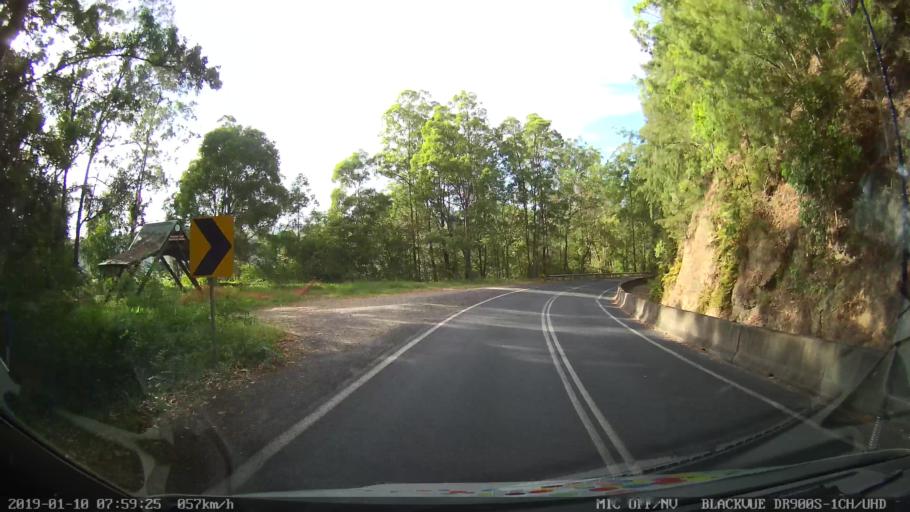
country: AU
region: New South Wales
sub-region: Bellingen
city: Dorrigo
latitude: -30.4209
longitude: 152.7789
